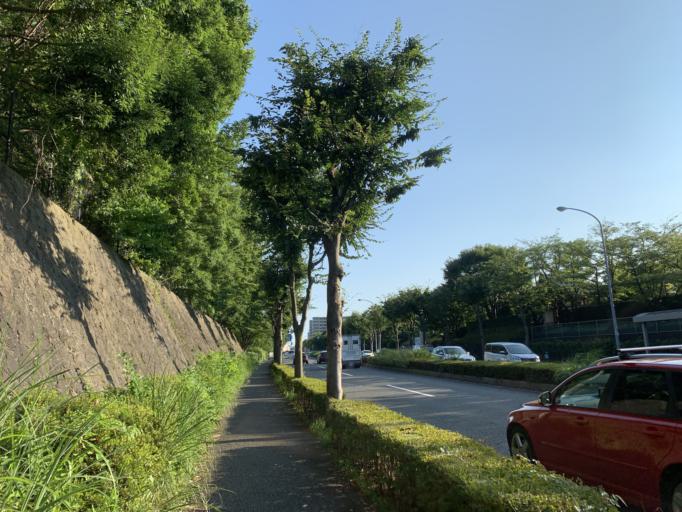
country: JP
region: Tokyo
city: Chofugaoka
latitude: 35.5608
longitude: 139.5797
